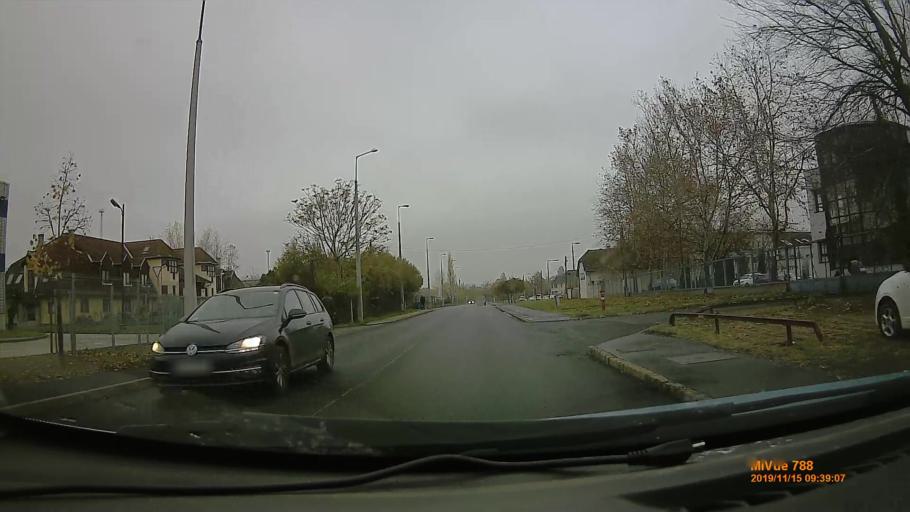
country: HU
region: Budapest
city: Budapest XX. keruelet
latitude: 47.4576
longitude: 19.1031
